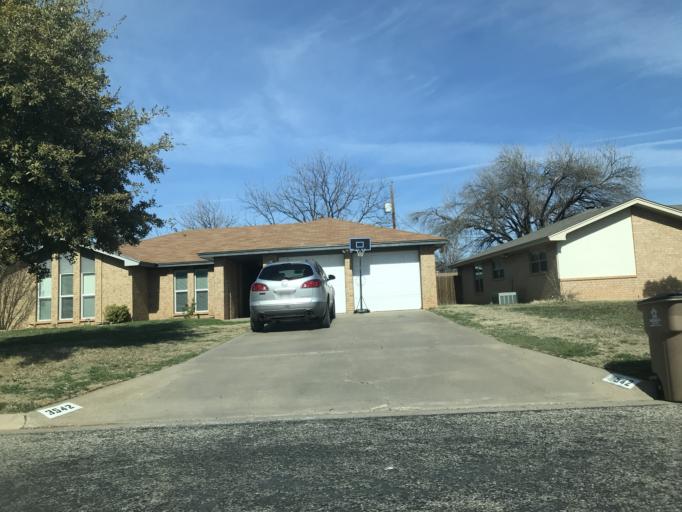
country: US
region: Texas
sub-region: Tom Green County
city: San Angelo
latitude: 31.4375
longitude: -100.4847
